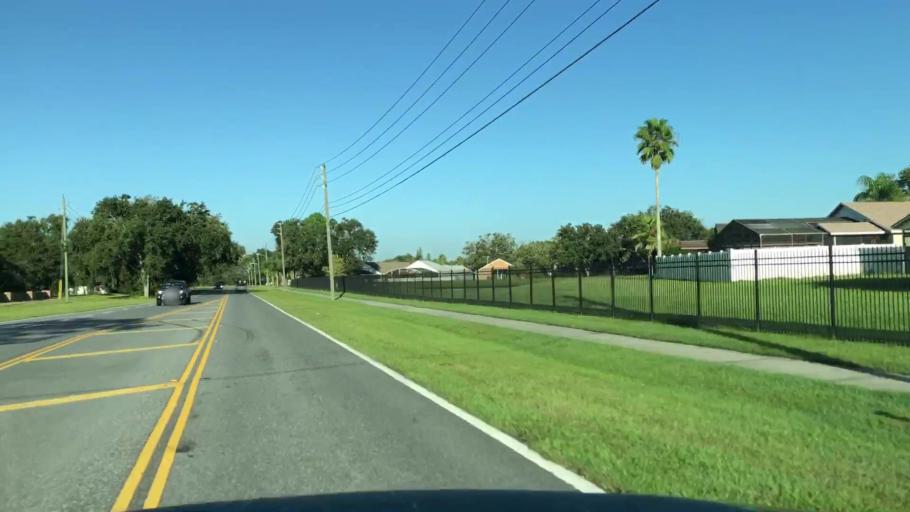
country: US
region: Florida
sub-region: Osceola County
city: Celebration
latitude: 28.3186
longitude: -81.4769
